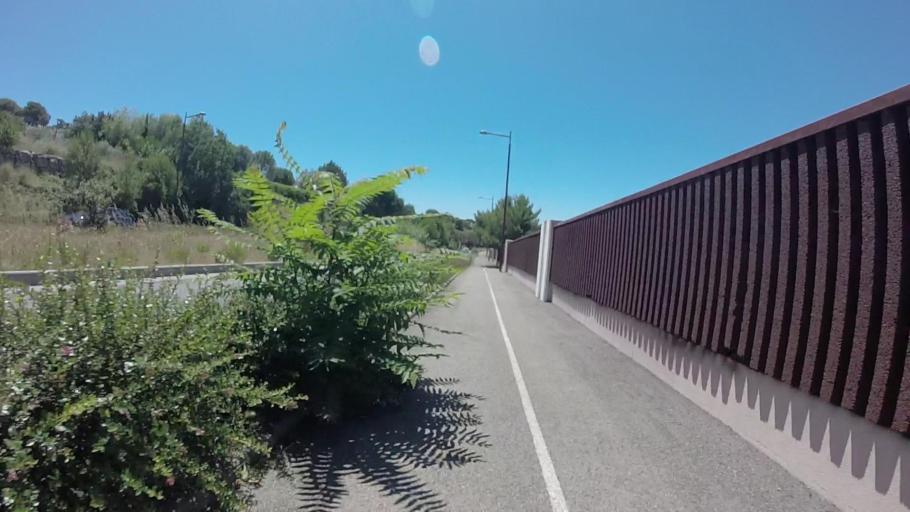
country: FR
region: Provence-Alpes-Cote d'Azur
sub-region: Departement des Alpes-Maritimes
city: Biot
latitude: 43.5916
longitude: 7.0920
